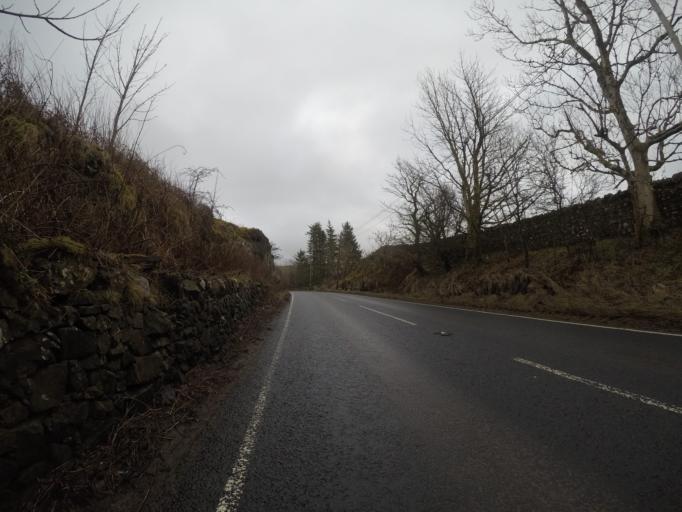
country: GB
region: Scotland
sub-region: North Ayrshire
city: Fairlie
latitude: 55.7764
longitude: -4.8403
